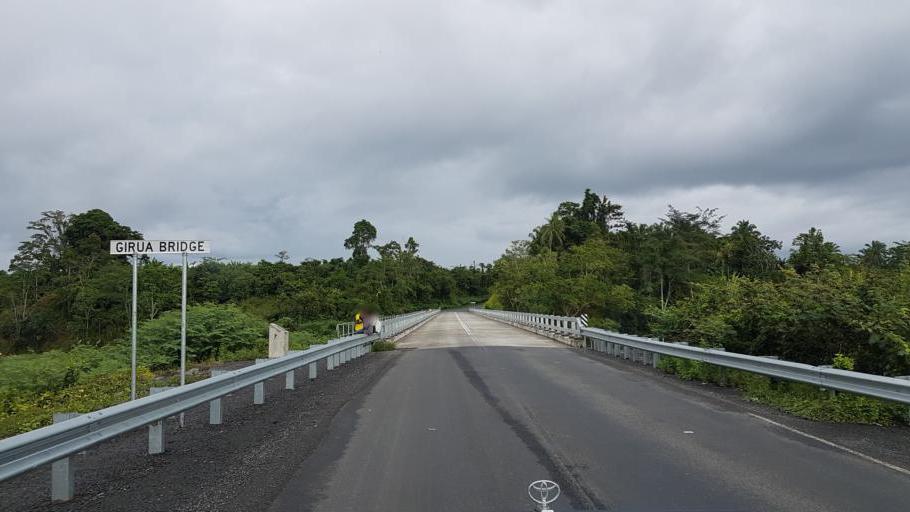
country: PG
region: Northern Province
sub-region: Sohe
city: Popondetta
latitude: -8.8372
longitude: 148.2731
